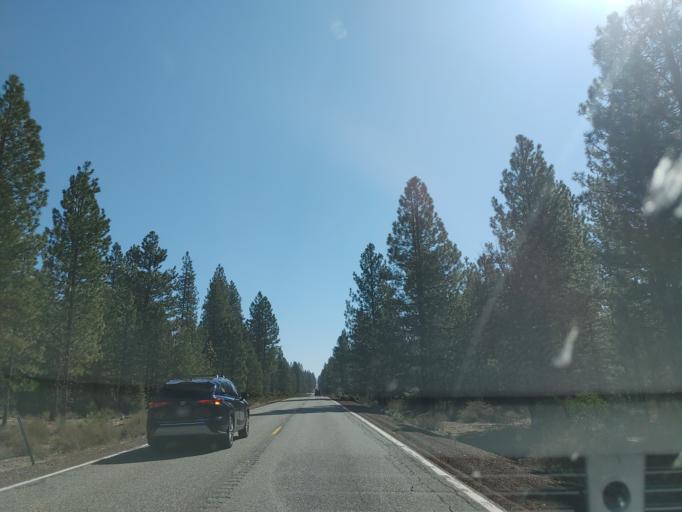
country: US
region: California
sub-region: Siskiyou County
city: McCloud
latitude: 41.2536
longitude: -122.0850
